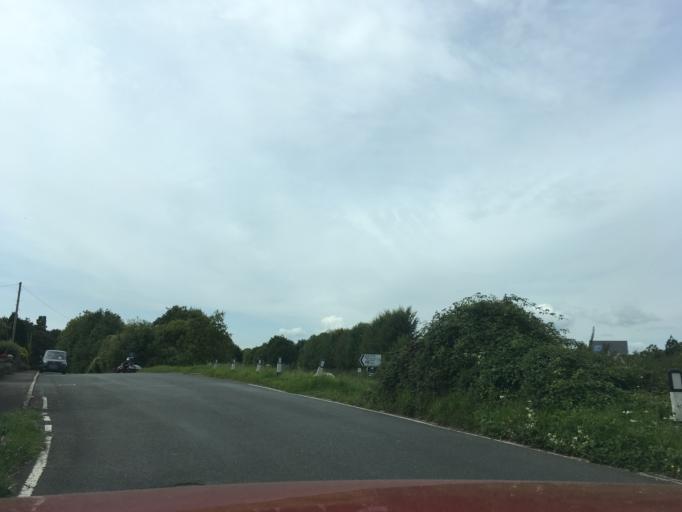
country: GB
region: England
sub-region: South Gloucestershire
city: Falfield
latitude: 51.6602
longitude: -2.4489
